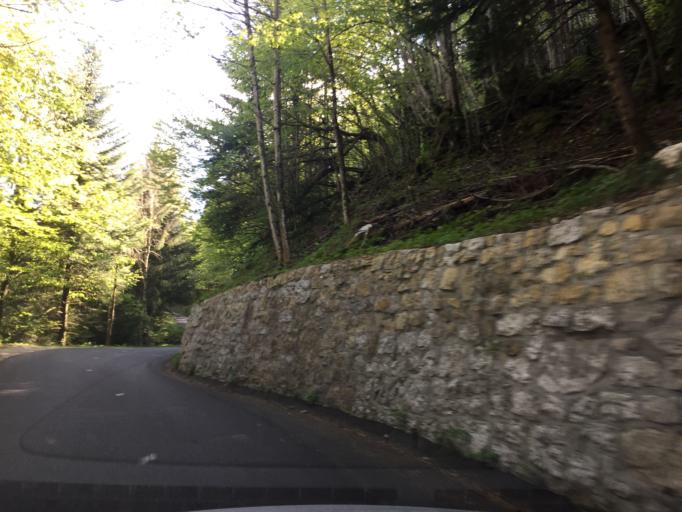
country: FR
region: Rhone-Alpes
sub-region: Departement de la Savoie
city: La Motte-Servolex
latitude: 45.5908
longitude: 5.8278
